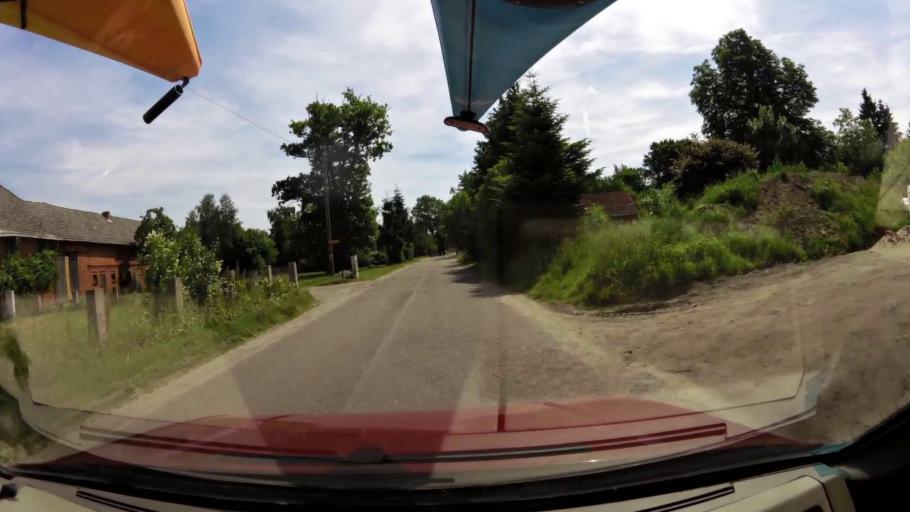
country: PL
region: West Pomeranian Voivodeship
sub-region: Powiat slawienski
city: Darlowo
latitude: 54.3192
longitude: 16.4116
